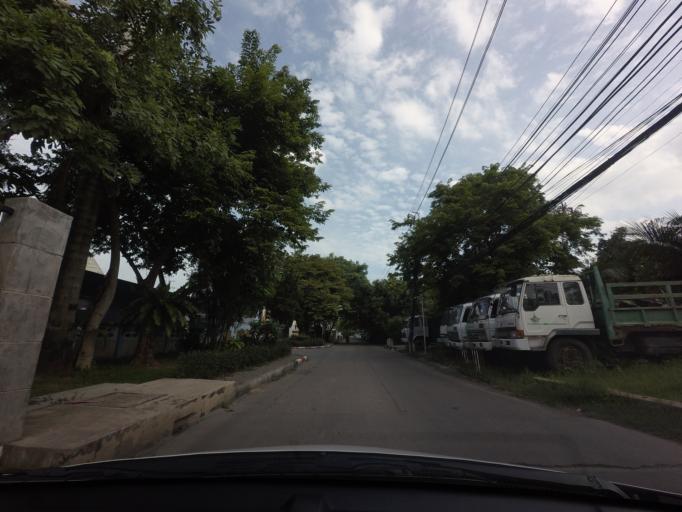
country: TH
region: Bangkok
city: Chatuchak
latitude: 13.8501
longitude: 100.5764
